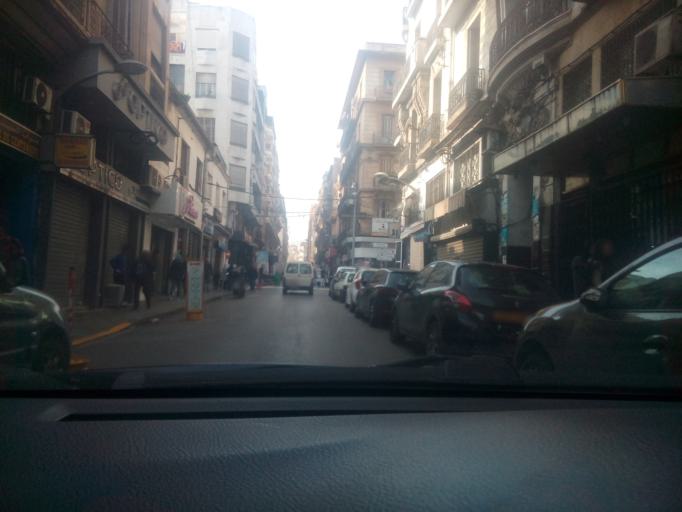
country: DZ
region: Oran
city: Oran
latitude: 35.7030
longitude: -0.6435
